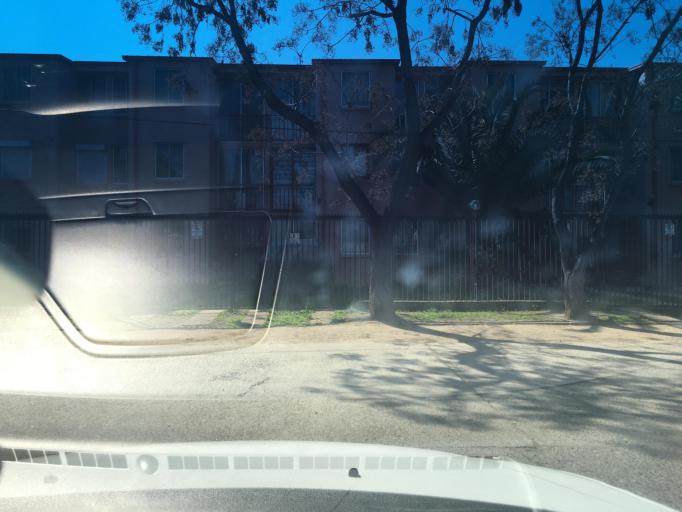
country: CL
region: Santiago Metropolitan
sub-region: Provincia de Santiago
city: Villa Presidente Frei, Nunoa, Santiago, Chile
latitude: -33.4670
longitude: -70.5782
